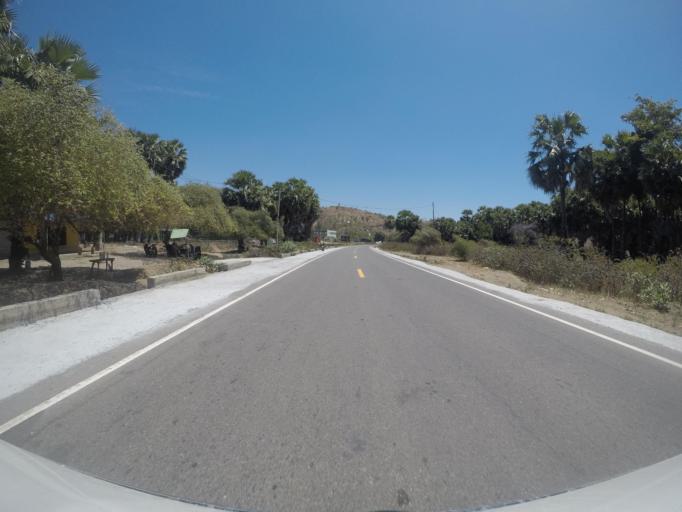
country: ID
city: Metinaro
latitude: -8.5376
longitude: 125.7034
